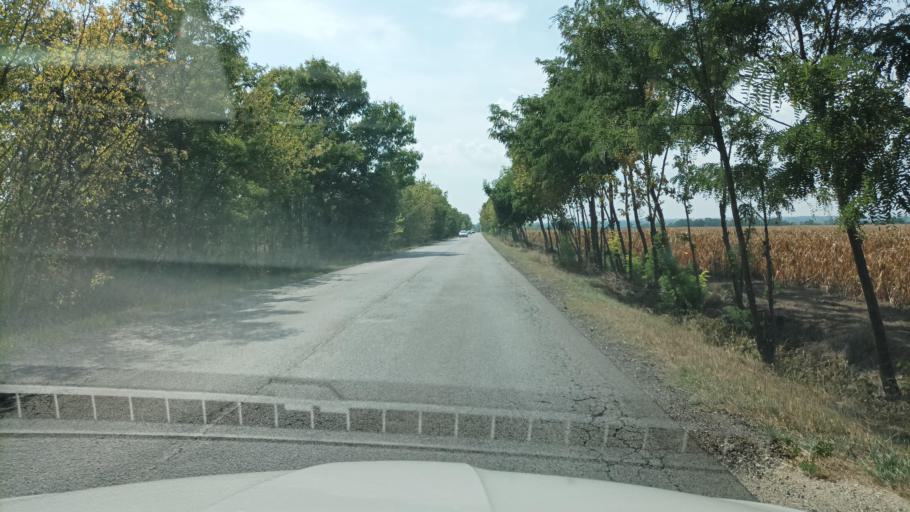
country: HU
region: Pest
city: Tura
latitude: 47.6262
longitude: 19.6218
